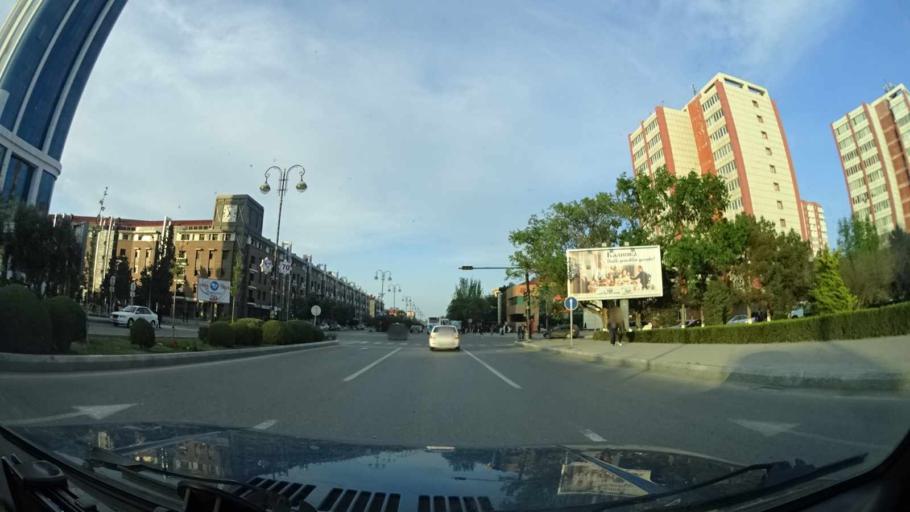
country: AZ
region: Sumqayit
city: Sumqayit
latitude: 40.5852
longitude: 49.6661
